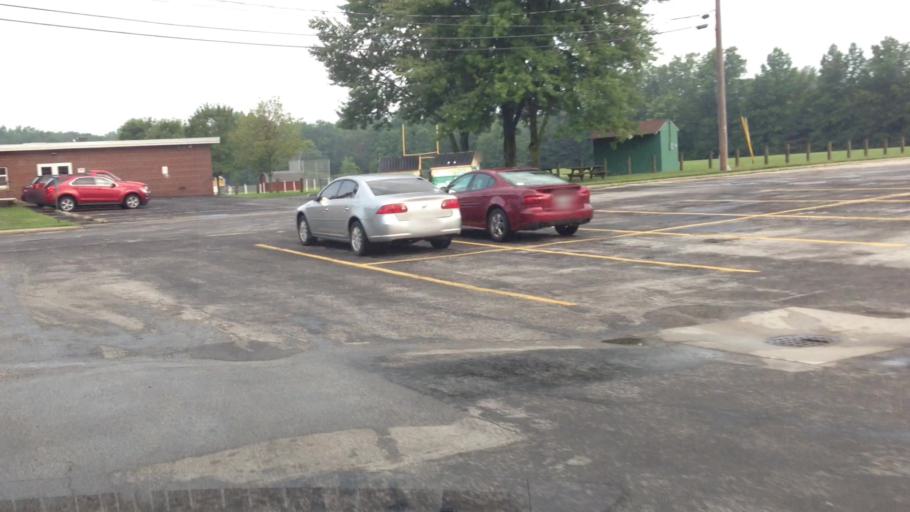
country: US
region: Ohio
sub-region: Cuyahoga County
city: Olmsted Falls
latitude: 41.3736
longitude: -81.9118
